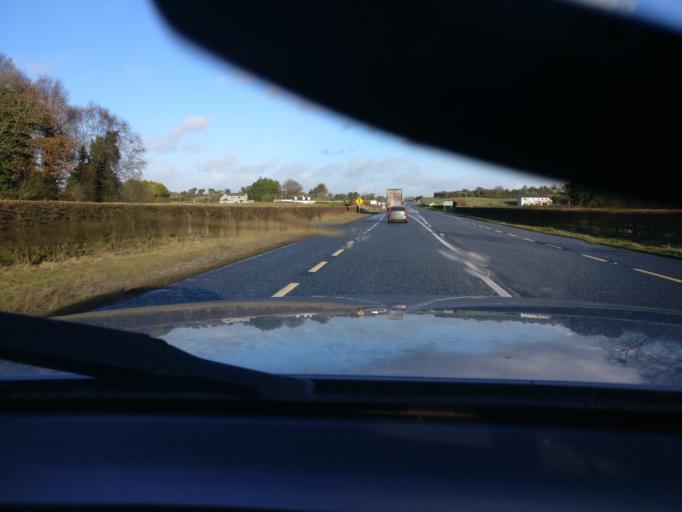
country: IE
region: Leinster
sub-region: An Iarmhi
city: Rathwire
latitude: 53.5943
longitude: -7.1166
